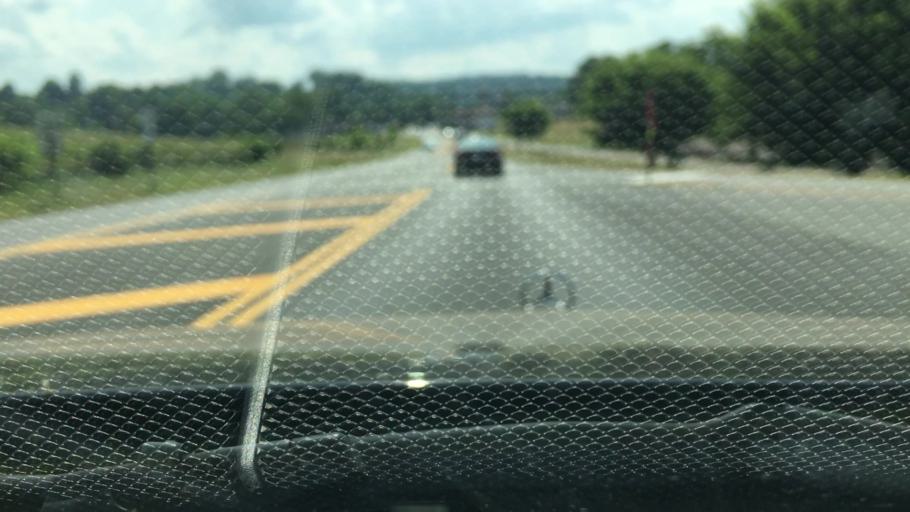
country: US
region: Virginia
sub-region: Orange County
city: Orange
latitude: 38.2423
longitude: -78.0985
